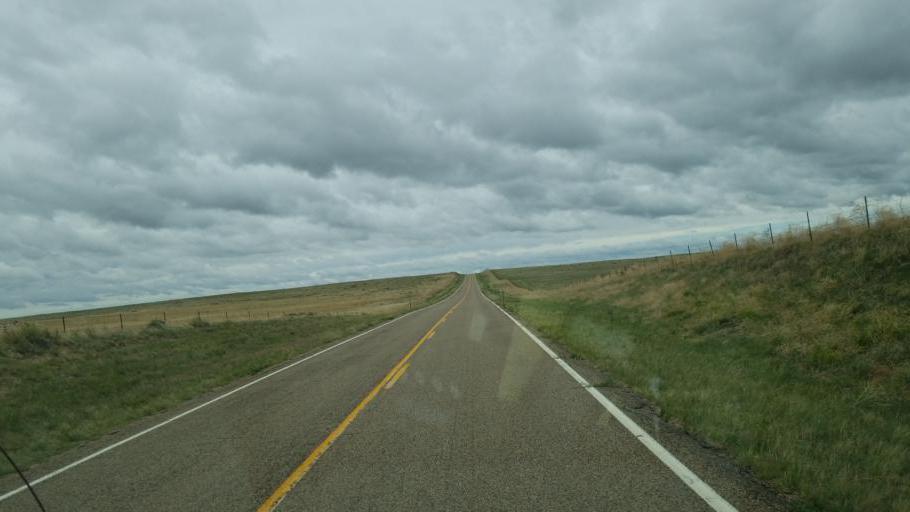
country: US
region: Colorado
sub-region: Lincoln County
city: Hugo
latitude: 38.8508
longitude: -103.5750
